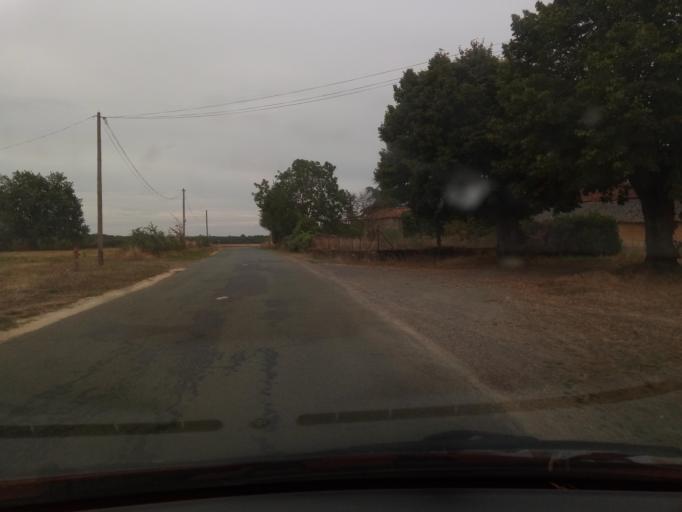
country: FR
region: Poitou-Charentes
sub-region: Departement de la Vienne
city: Saint-Savin
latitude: 46.5368
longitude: 0.7811
